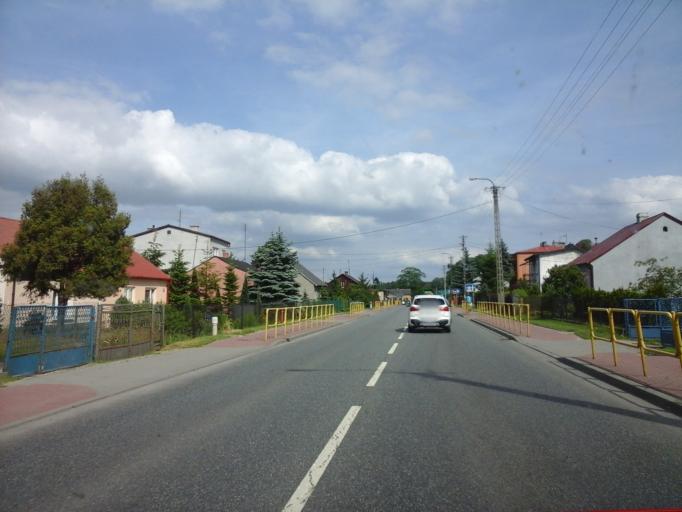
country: PL
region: Lodz Voivodeship
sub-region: Powiat opoczynski
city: Paradyz
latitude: 51.3062
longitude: 20.1117
